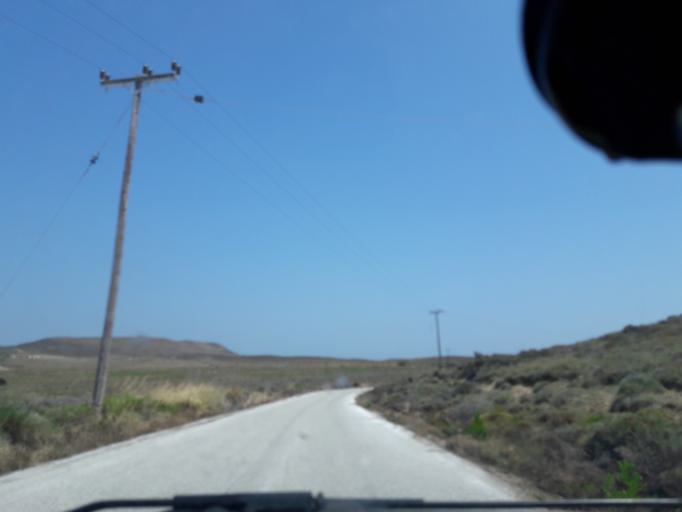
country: GR
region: North Aegean
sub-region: Nomos Lesvou
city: Myrina
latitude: 39.9749
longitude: 25.3537
